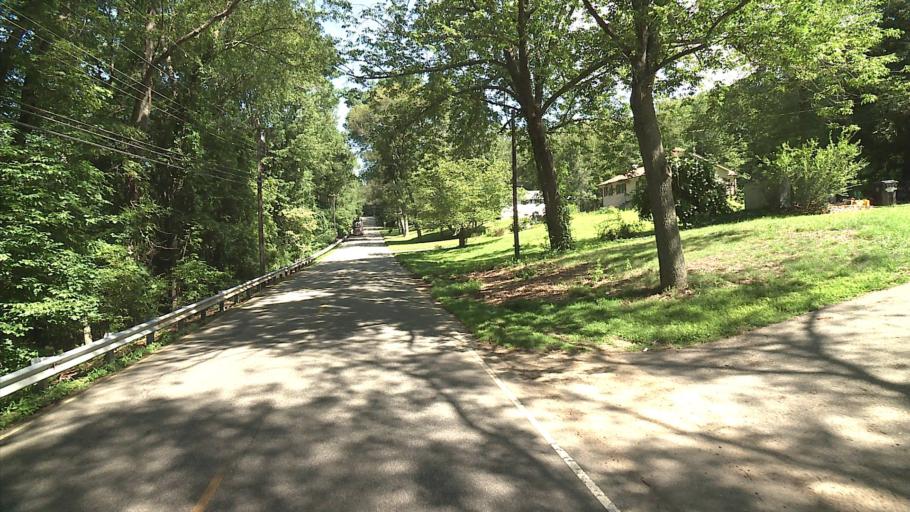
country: US
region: Connecticut
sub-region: New London County
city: Baltic
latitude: 41.6295
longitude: -72.0854
